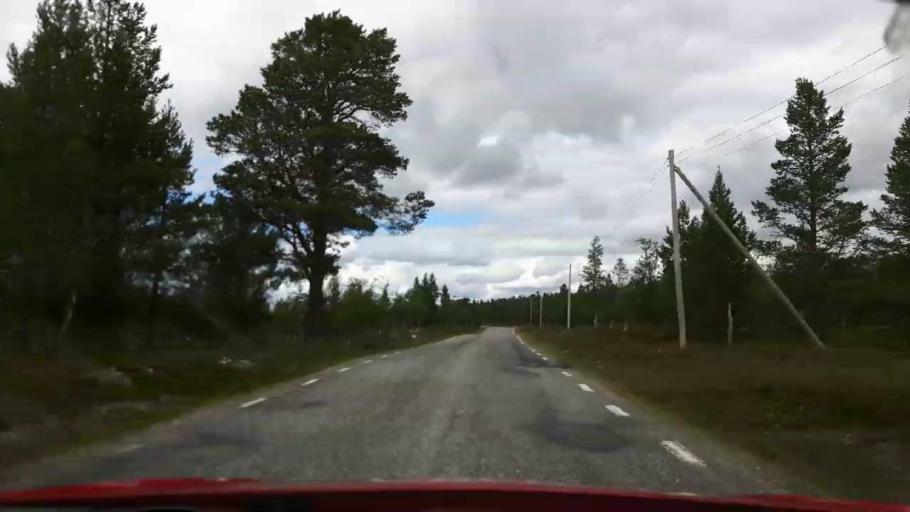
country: NO
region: Hedmark
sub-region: Engerdal
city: Engerdal
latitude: 62.3261
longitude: 12.8083
